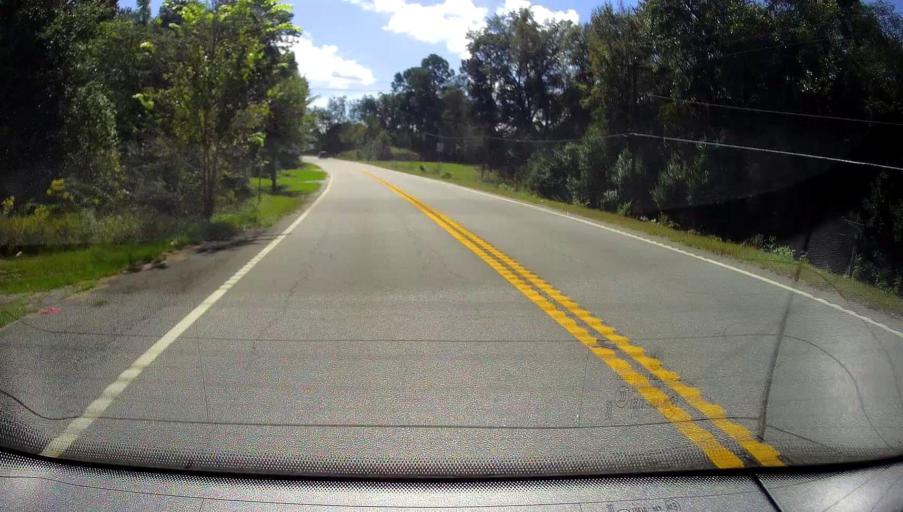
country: US
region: Georgia
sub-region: Bibb County
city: Macon
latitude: 32.8372
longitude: -83.5756
